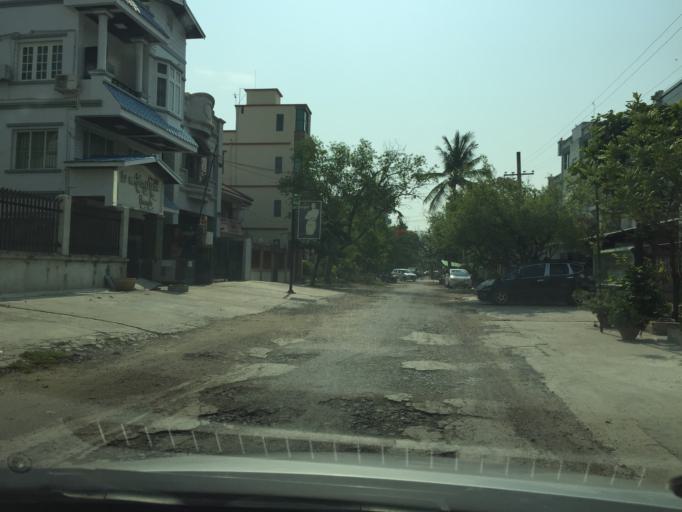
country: MM
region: Mandalay
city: Mandalay
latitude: 21.9722
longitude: 96.0974
